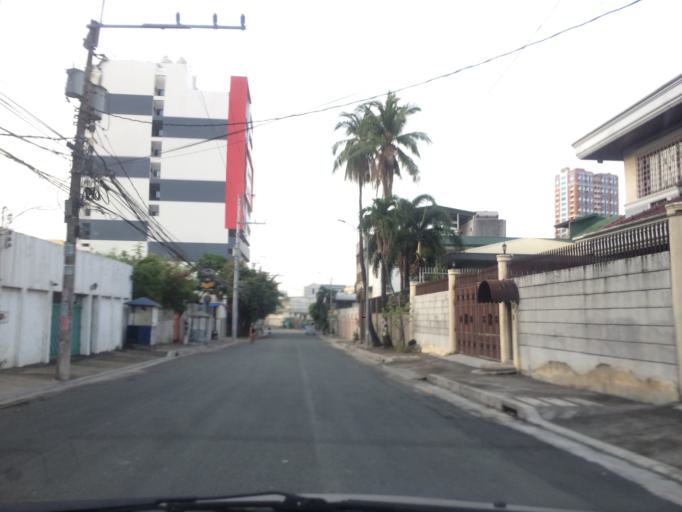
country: PH
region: Calabarzon
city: Del Monte
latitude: 14.6351
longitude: 121.0039
